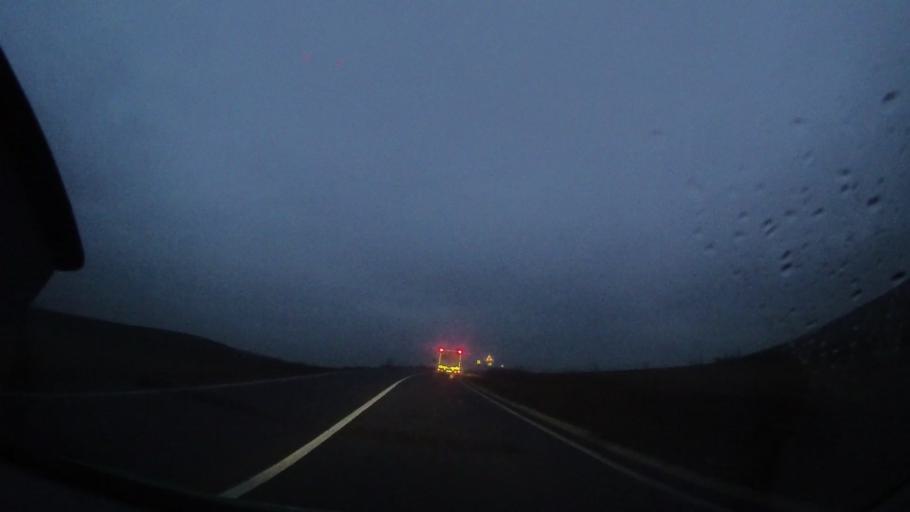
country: RO
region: Harghita
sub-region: Comuna Subcetate
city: Subcetate
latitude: 46.8453
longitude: 25.4713
